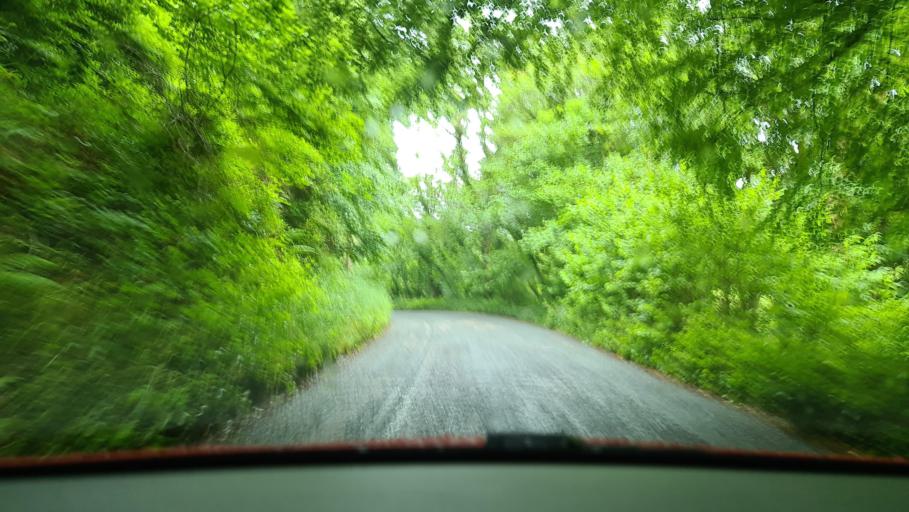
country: GB
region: England
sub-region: Cornwall
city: Liskeard
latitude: 50.4654
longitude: -4.5591
